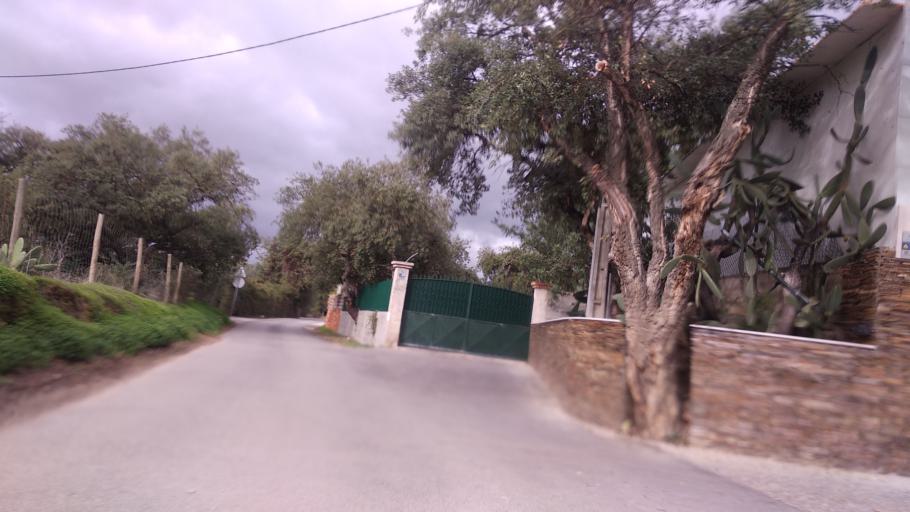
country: PT
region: Faro
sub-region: Loule
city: Almancil
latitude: 37.0981
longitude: -8.0457
